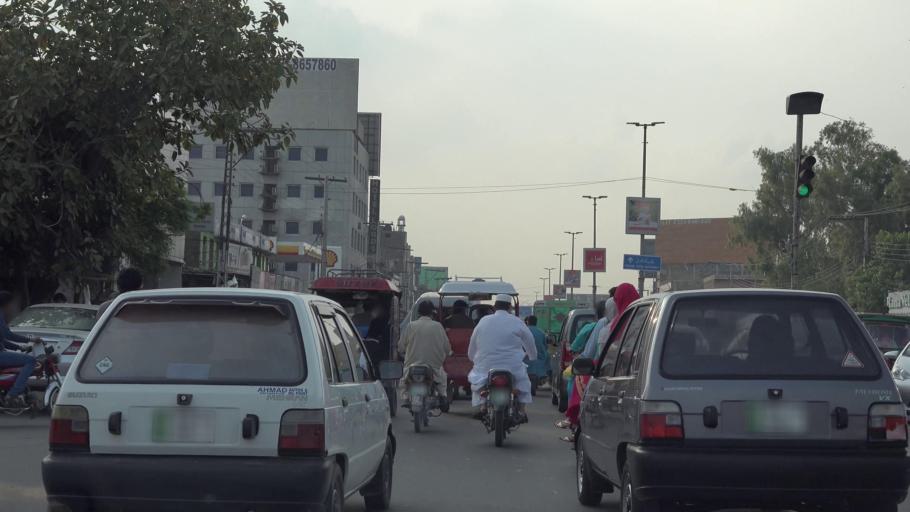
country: PK
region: Punjab
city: Faisalabad
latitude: 31.4168
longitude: 73.1084
